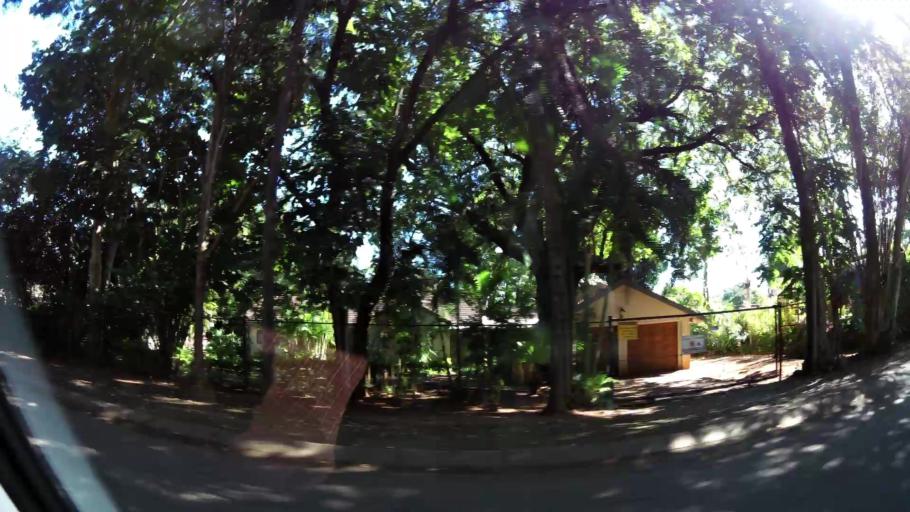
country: ZA
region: Limpopo
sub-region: Mopani District Municipality
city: Tzaneen
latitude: -23.8319
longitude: 30.1513
